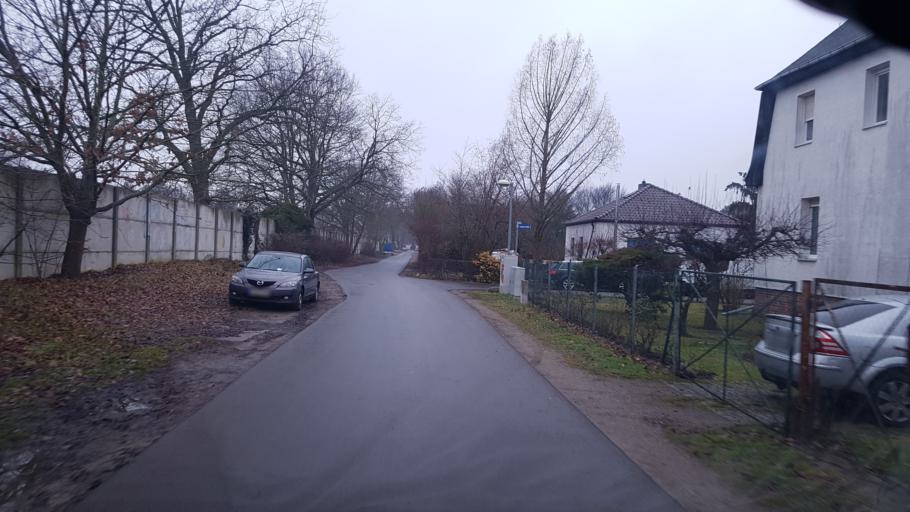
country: DE
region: Brandenburg
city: Stahnsdorf
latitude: 52.3755
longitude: 13.2114
